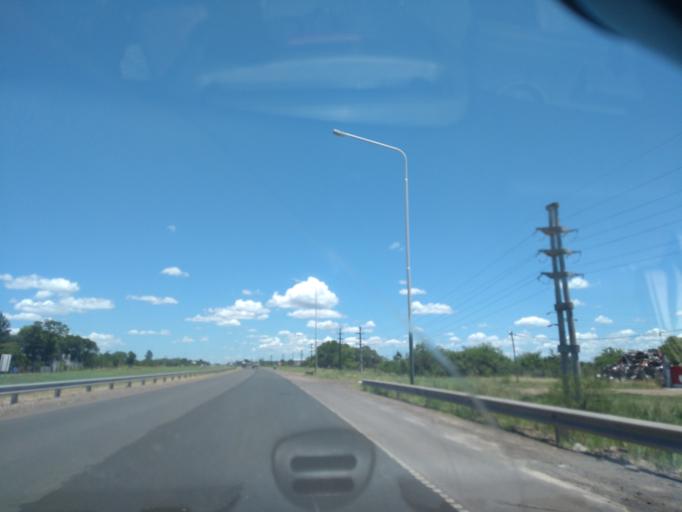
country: AR
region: Chaco
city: Fontana
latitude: -27.3881
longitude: -59.0286
